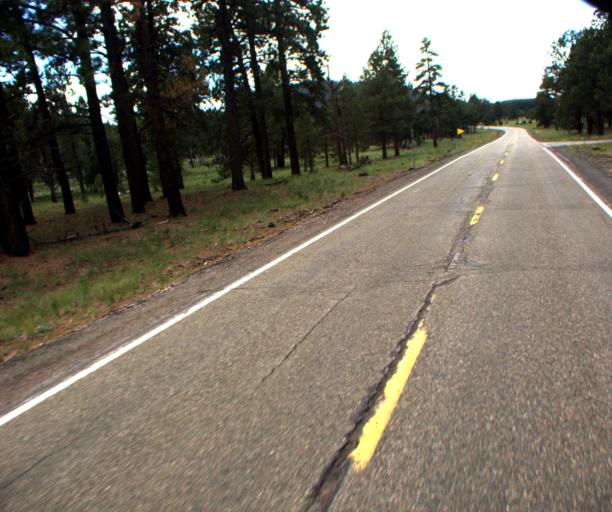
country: US
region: Arizona
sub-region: Coconino County
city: Parks
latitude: 35.3807
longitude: -111.7844
